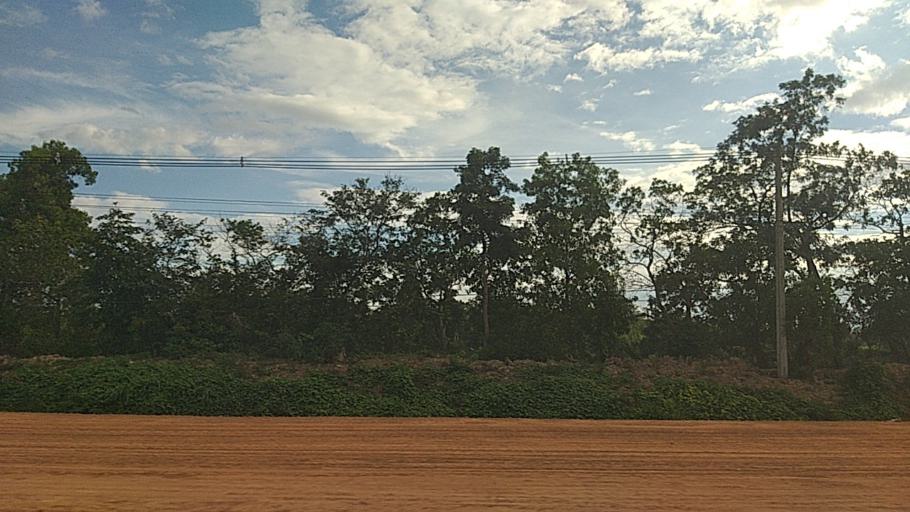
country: TH
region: Surin
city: Kap Choeng
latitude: 14.5026
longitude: 103.5611
